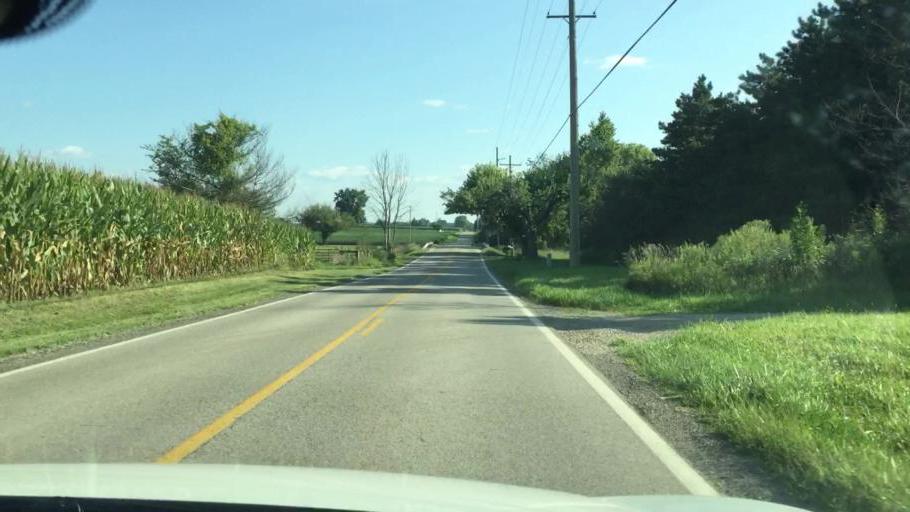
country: US
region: Ohio
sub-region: Clark County
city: Northridge
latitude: 39.9511
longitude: -83.7093
